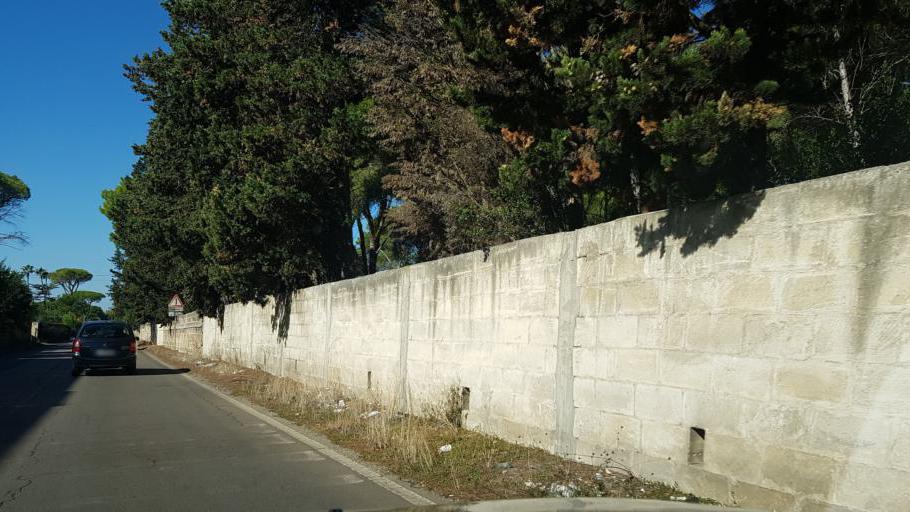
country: IT
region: Apulia
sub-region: Provincia di Lecce
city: San Pietro in Lama
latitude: 40.3385
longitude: 18.1232
